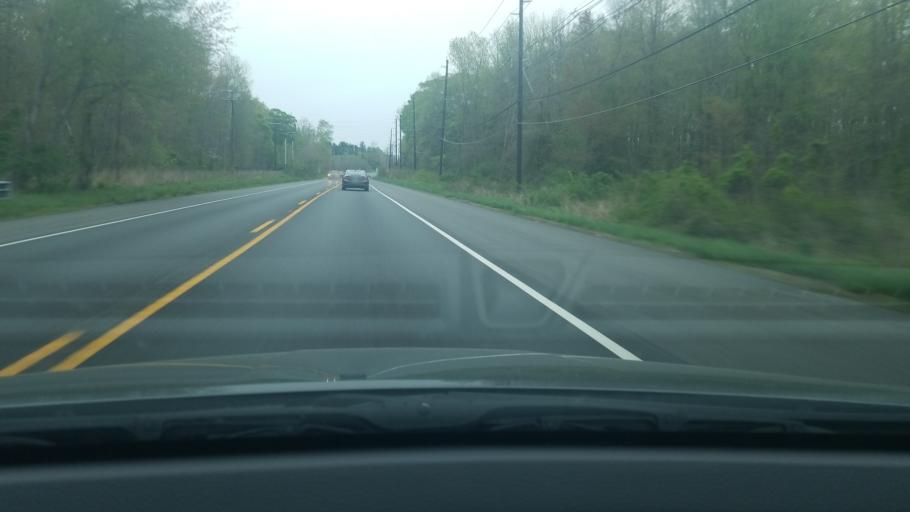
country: US
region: New Jersey
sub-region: Burlington County
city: Medford Lakes
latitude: 39.9013
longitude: -74.7979
